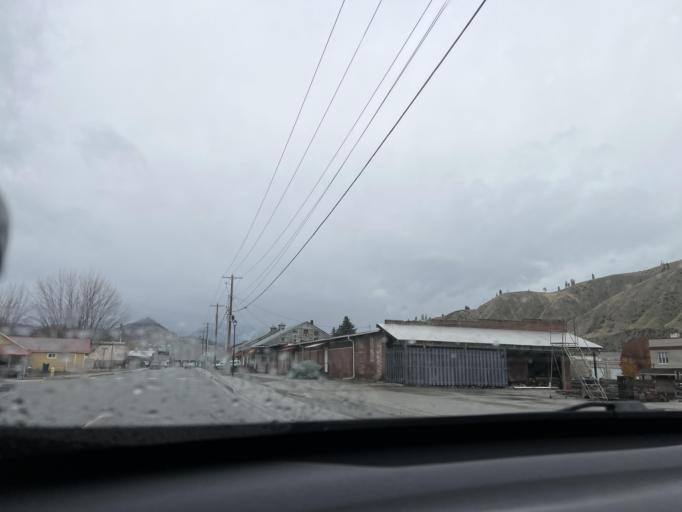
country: US
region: Washington
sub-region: Chelan County
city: Cashmere
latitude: 47.5202
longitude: -120.4672
